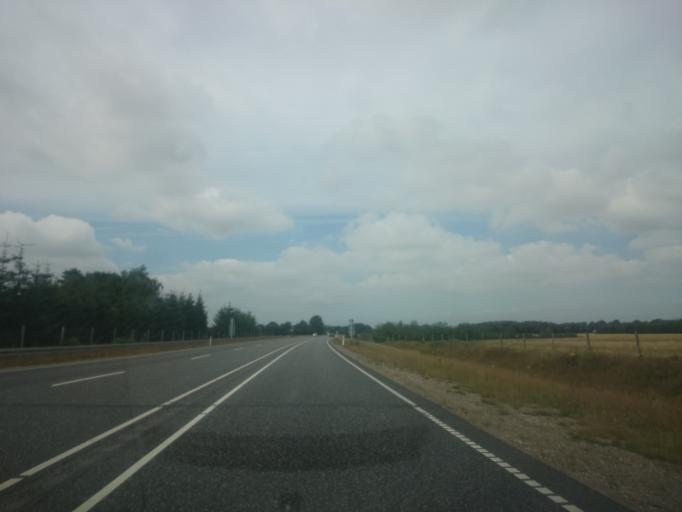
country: DK
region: South Denmark
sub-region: Vejle Kommune
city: Egtved
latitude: 55.7082
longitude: 9.2363
